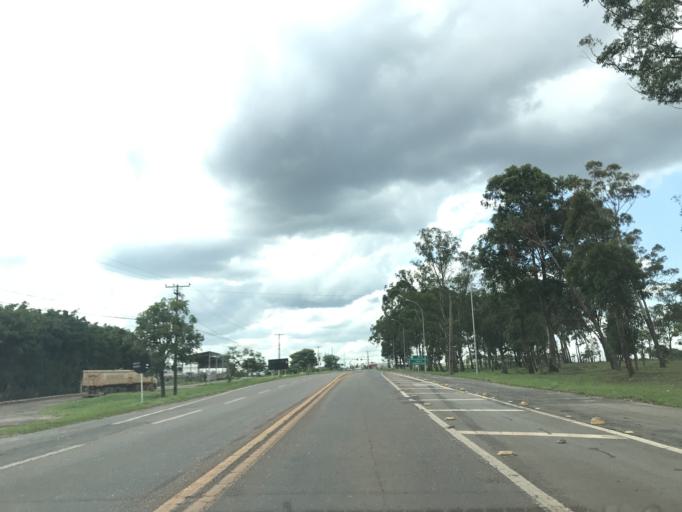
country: BR
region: Federal District
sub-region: Brasilia
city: Brasilia
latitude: -15.6896
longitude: -47.8565
